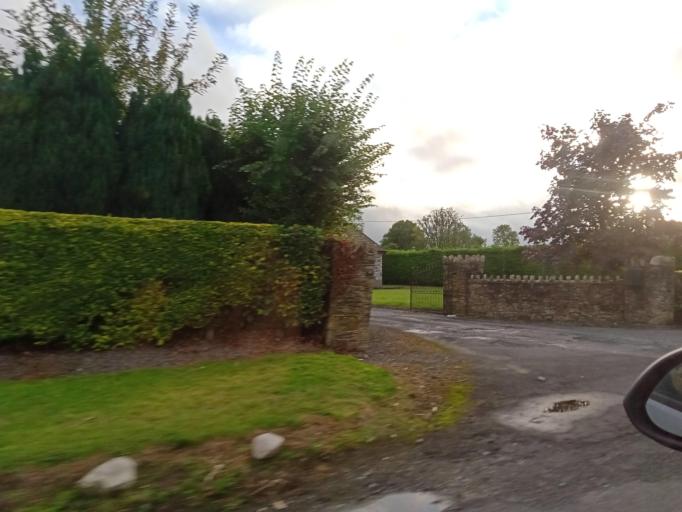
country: IE
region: Leinster
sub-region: Laois
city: Mountmellick
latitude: 53.1417
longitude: -7.4237
